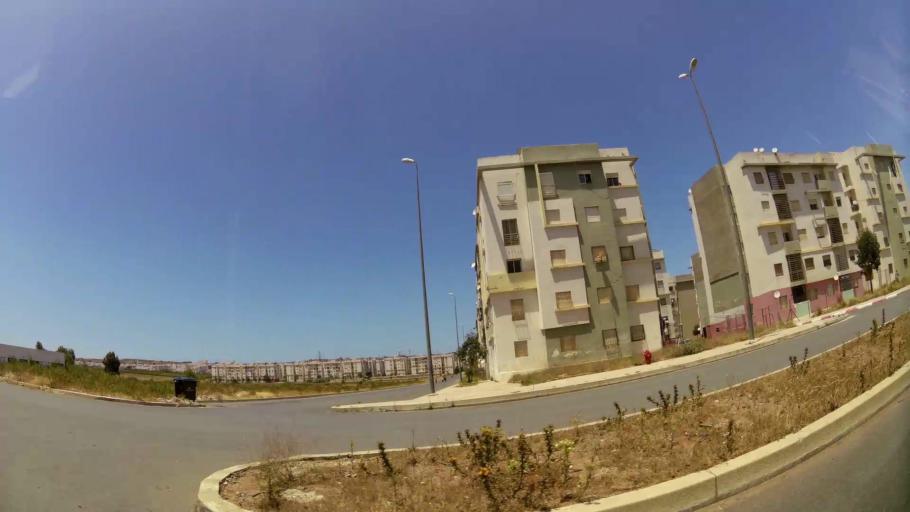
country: MA
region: Gharb-Chrarda-Beni Hssen
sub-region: Kenitra Province
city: Kenitra
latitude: 34.2481
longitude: -6.6363
